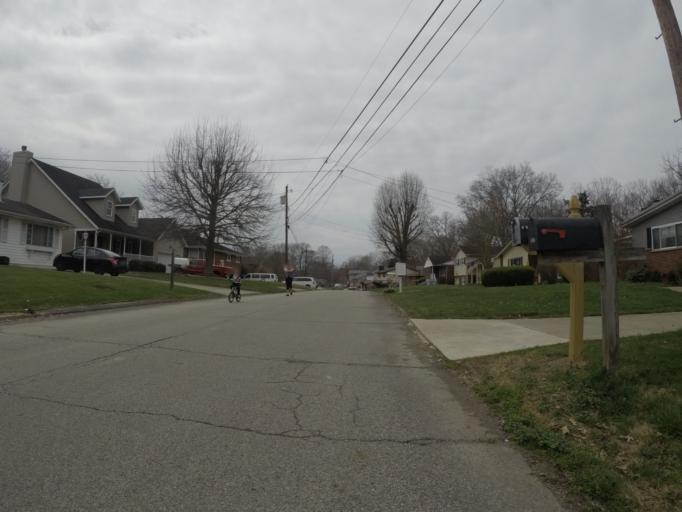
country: US
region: West Virginia
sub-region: Cabell County
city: Pea Ridge
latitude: 38.4213
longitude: -82.3218
